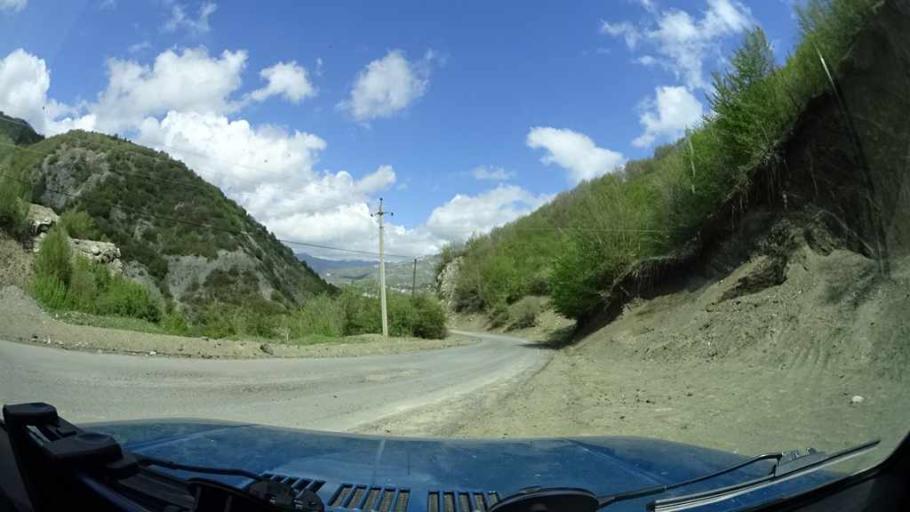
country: AZ
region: Ismayilli
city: Basqal
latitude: 40.8400
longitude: 48.3634
